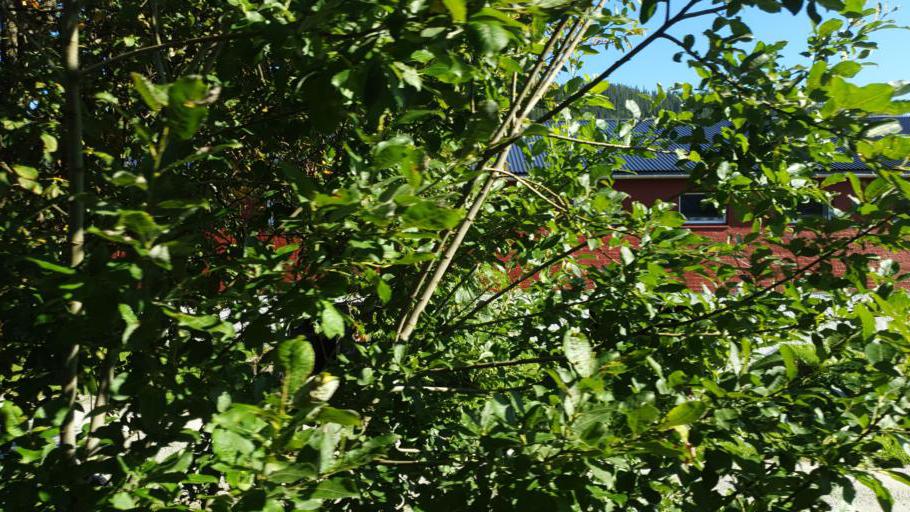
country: NO
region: Sor-Trondelag
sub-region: Orkdal
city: Orkanger
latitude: 63.2826
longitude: 9.8354
